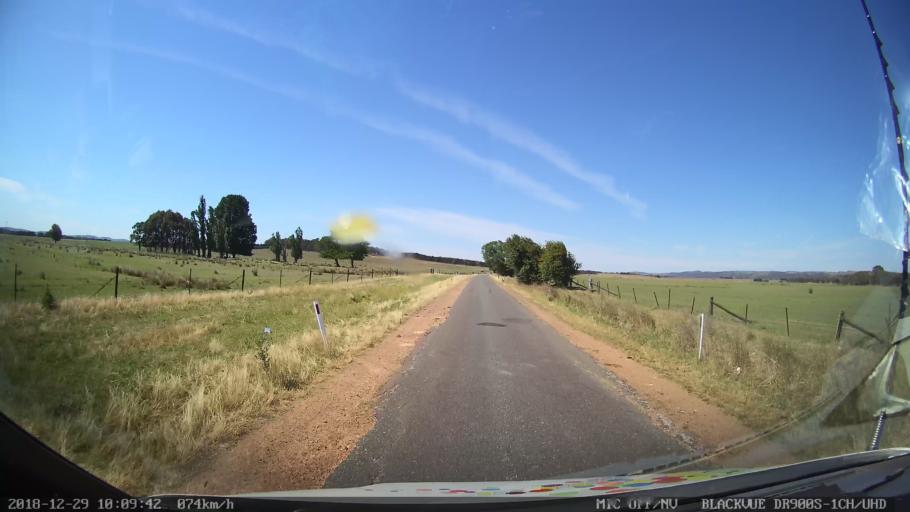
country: AU
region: New South Wales
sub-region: Yass Valley
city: Gundaroo
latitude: -34.8686
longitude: 149.4594
